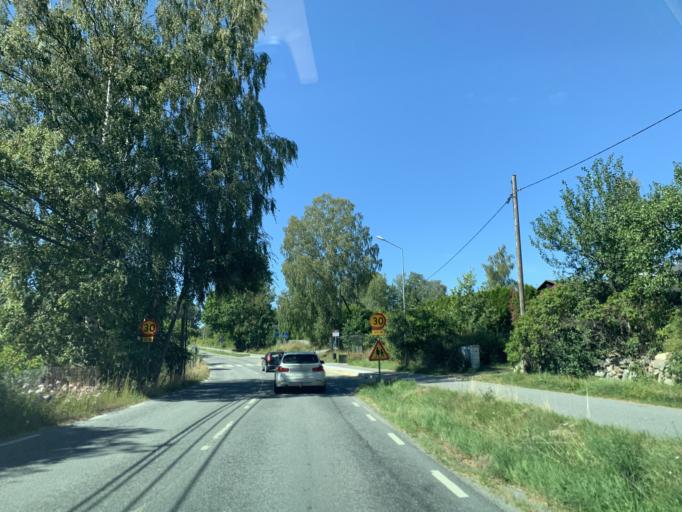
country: SE
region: Stockholm
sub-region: Ekero Kommun
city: Ekeroe
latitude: 59.2712
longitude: 17.8072
